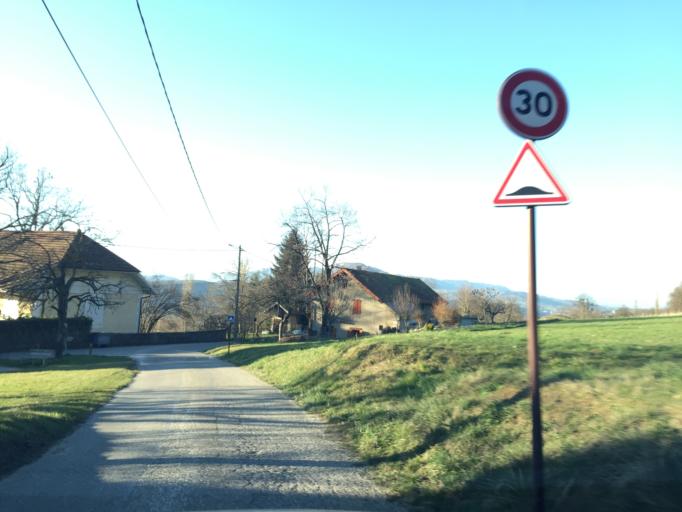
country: FR
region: Rhone-Alpes
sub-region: Departement de la Savoie
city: Mouxy
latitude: 45.6907
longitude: 5.9447
